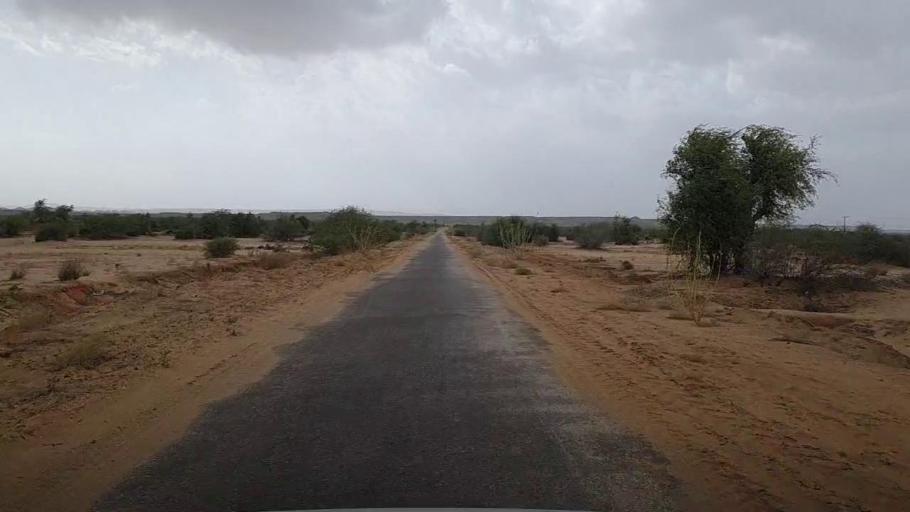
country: PK
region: Sindh
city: Jamshoro
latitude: 25.4040
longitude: 67.7081
